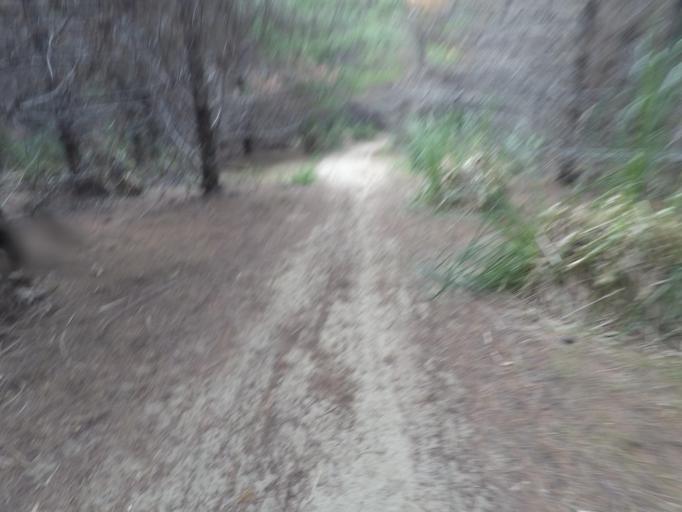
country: NZ
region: Auckland
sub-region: Auckland
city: Parakai
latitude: -36.6012
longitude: 174.2739
